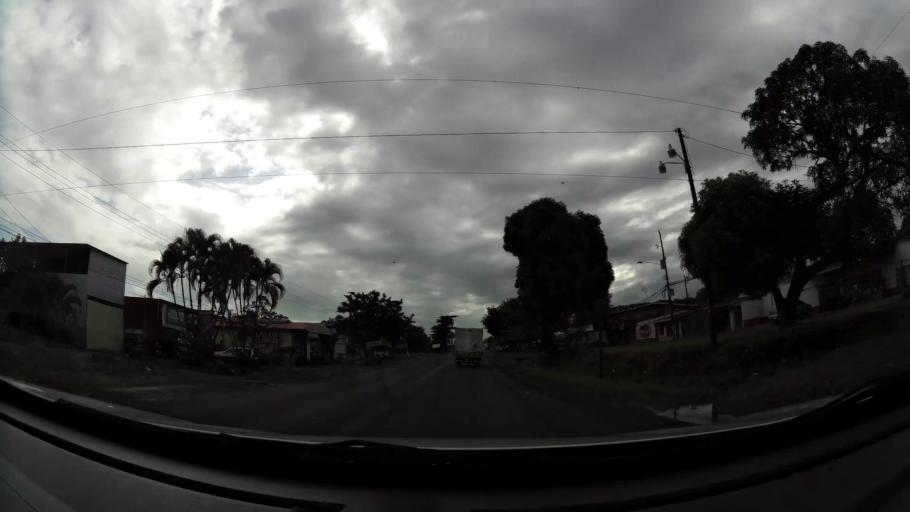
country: CR
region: Limon
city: Pocora
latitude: 10.1700
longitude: -83.6075
